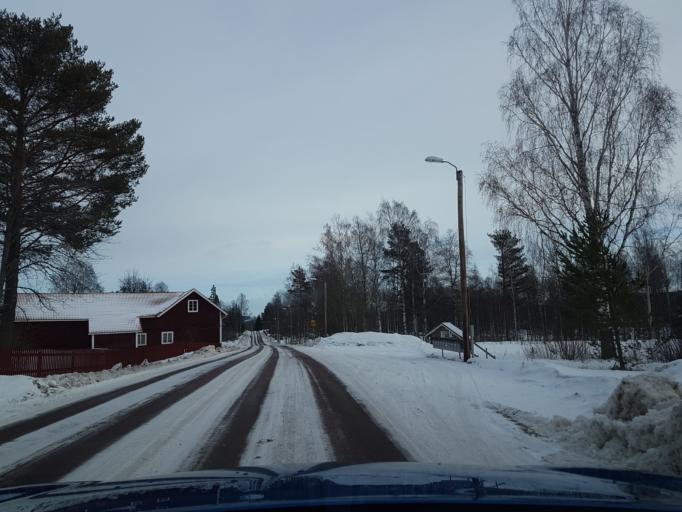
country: SE
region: Dalarna
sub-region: Leksand Municipality
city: Leksand
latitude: 60.7505
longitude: 15.0101
